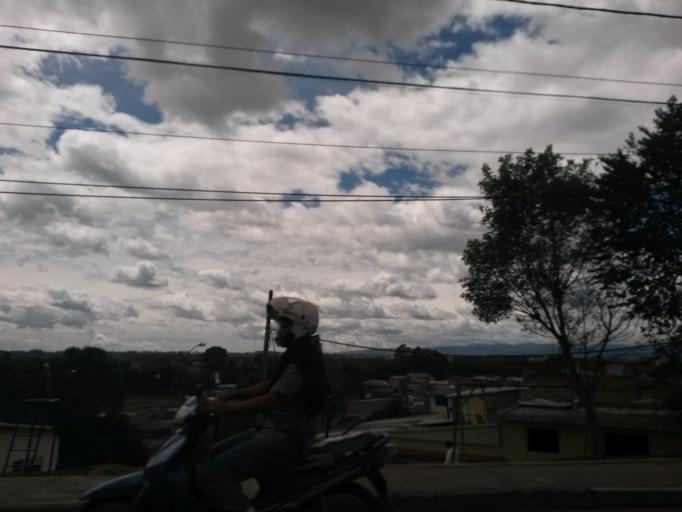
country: CO
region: Cauca
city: Popayan
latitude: 2.4415
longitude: -76.6249
